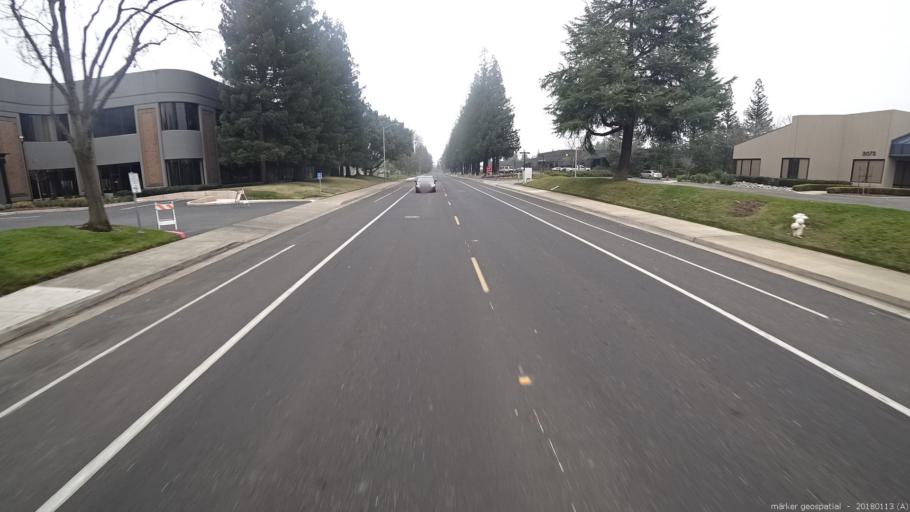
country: US
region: California
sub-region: Sacramento County
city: Rancho Cordova
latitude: 38.5917
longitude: -121.2707
